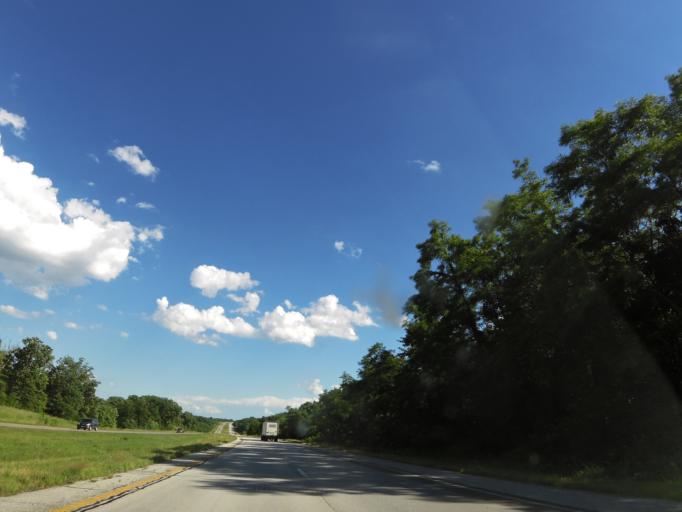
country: US
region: Missouri
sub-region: Lewis County
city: Canton
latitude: 40.0753
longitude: -91.5353
